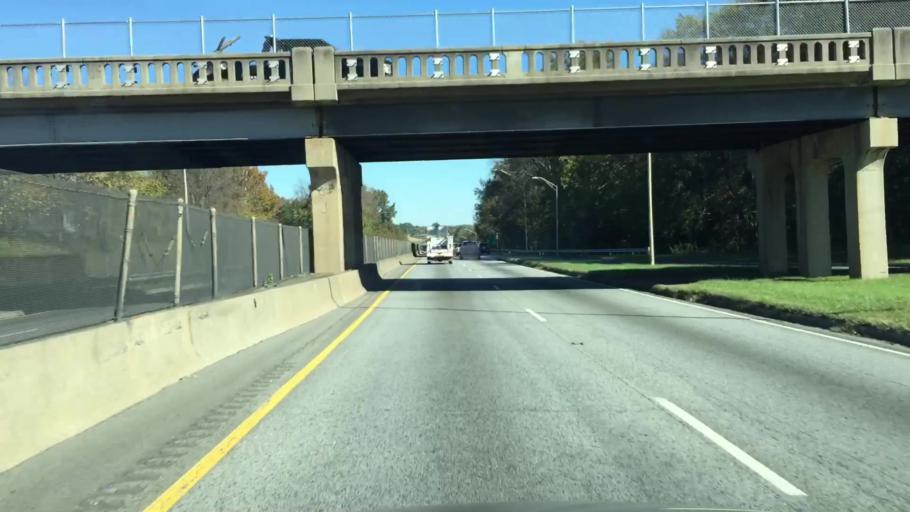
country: US
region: North Carolina
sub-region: Guilford County
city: Greensboro
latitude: 36.0998
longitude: -79.7647
